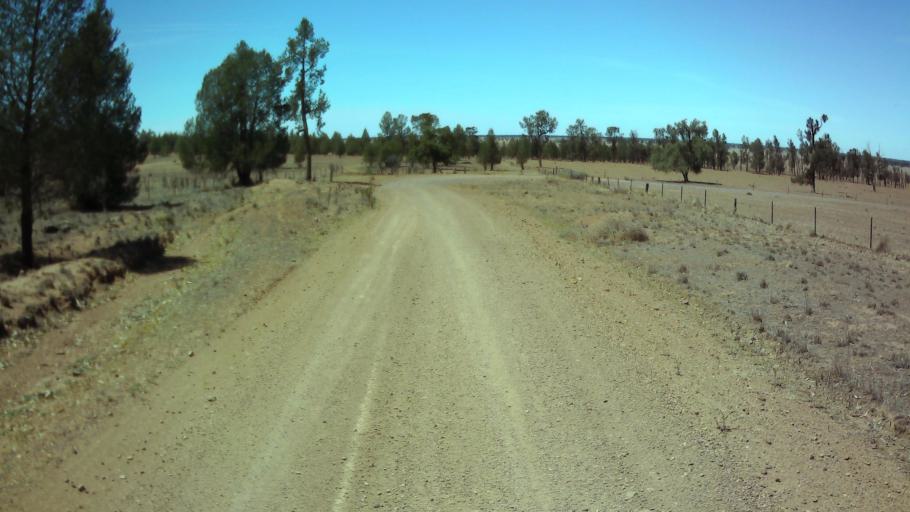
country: AU
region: New South Wales
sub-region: Forbes
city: Forbes
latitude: -33.7160
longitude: 147.6993
